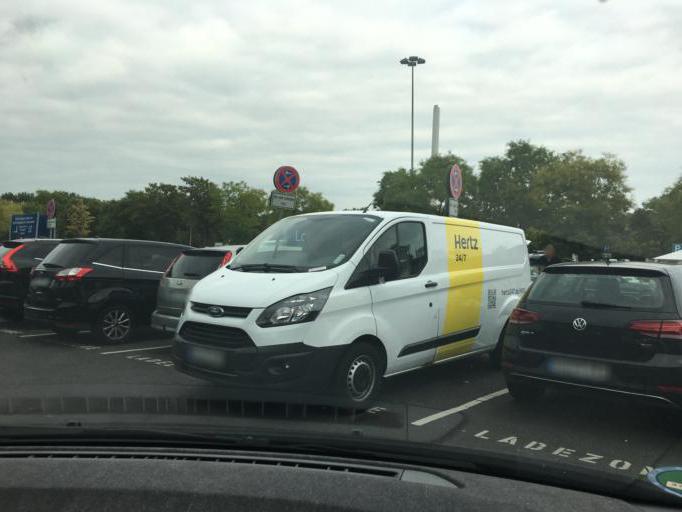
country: DE
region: North Rhine-Westphalia
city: Wesseling
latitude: 50.8620
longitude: 6.9718
